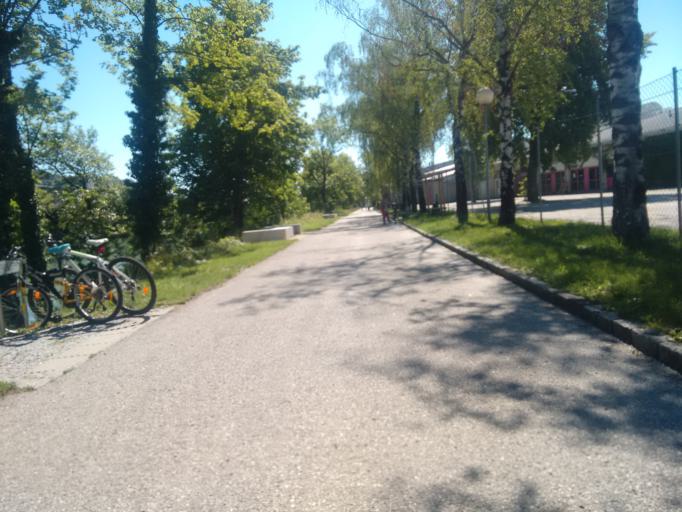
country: AT
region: Upper Austria
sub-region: Wels-Land
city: Thalheim bei Wels
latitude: 48.1530
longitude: 14.0242
